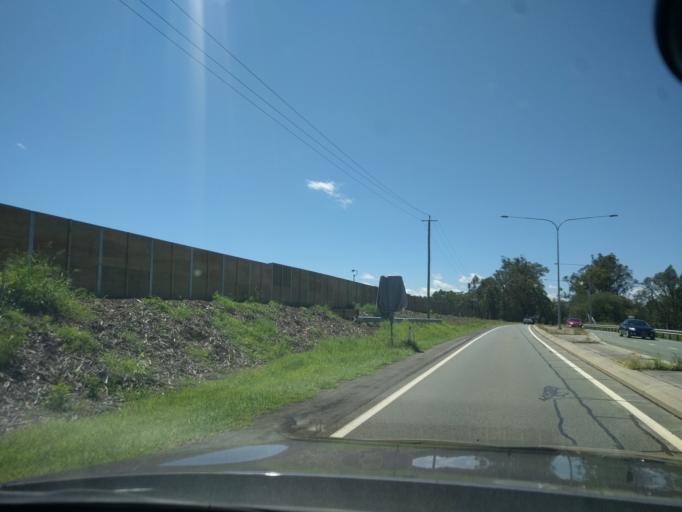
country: AU
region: Queensland
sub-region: Logan
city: Cedar Vale
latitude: -27.9592
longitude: 152.9927
